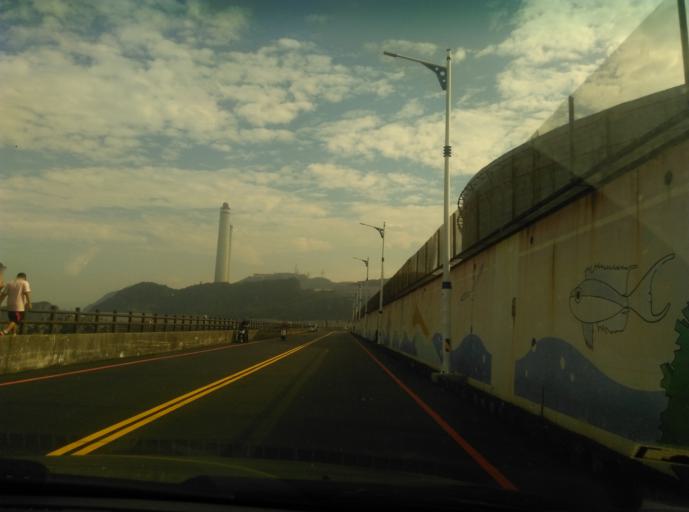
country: TW
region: Taiwan
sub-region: Keelung
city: Keelung
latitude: 25.1622
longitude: 121.7311
